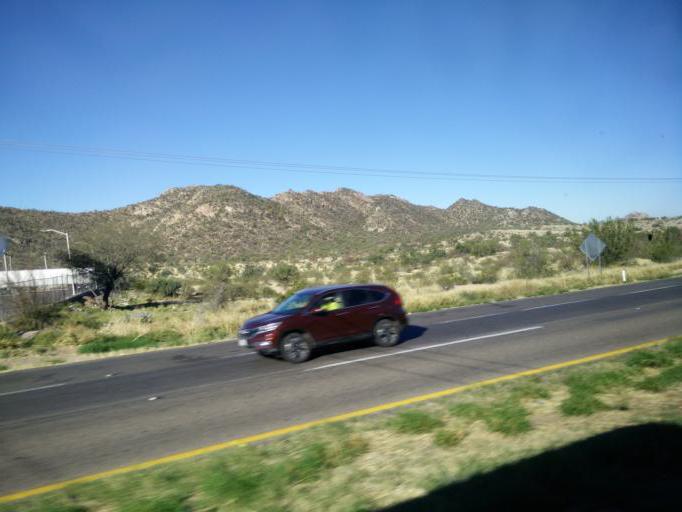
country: MX
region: Sonora
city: Hermosillo
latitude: 28.9889
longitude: -110.9705
